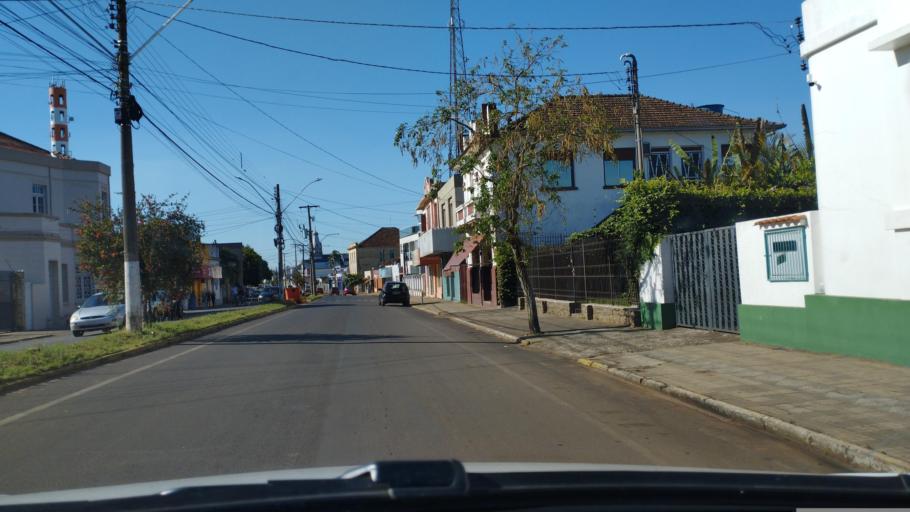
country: BR
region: Rio Grande do Sul
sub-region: Tupancireta
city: Tupancireta
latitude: -29.0839
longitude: -53.8357
